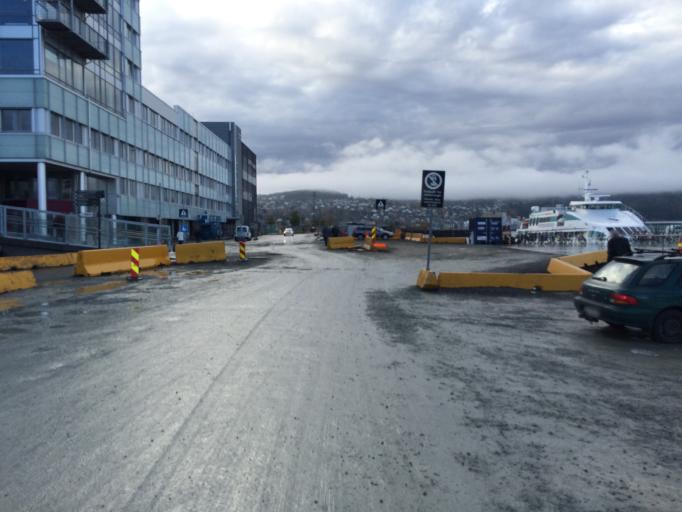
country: NO
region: Sor-Trondelag
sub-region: Trondheim
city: Trondheim
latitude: 63.4381
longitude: 10.3988
